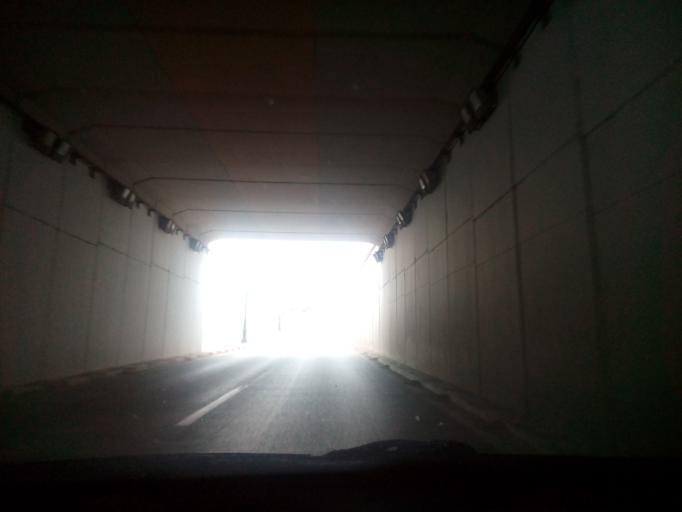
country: DZ
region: Tlemcen
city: Mansoura
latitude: 34.8939
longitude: -1.3559
